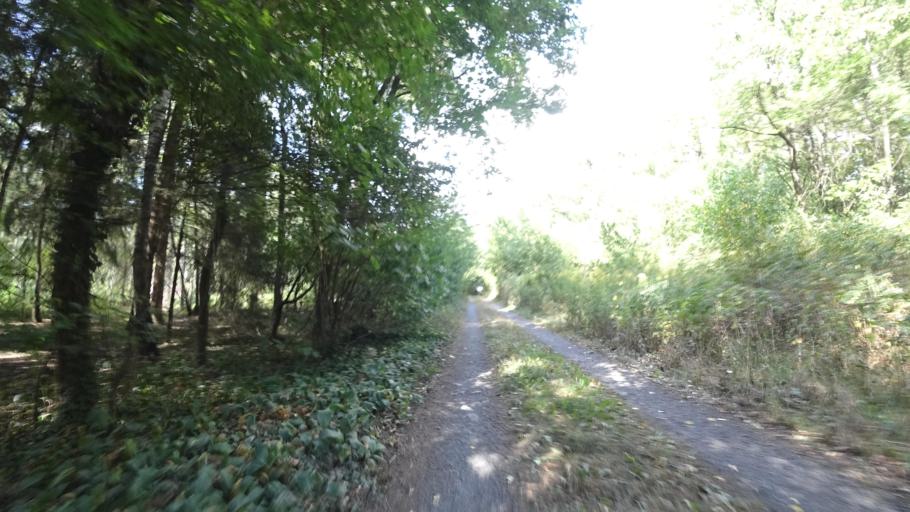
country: DE
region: North Rhine-Westphalia
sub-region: Regierungsbezirk Detmold
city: Verl
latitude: 51.9378
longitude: 8.5016
